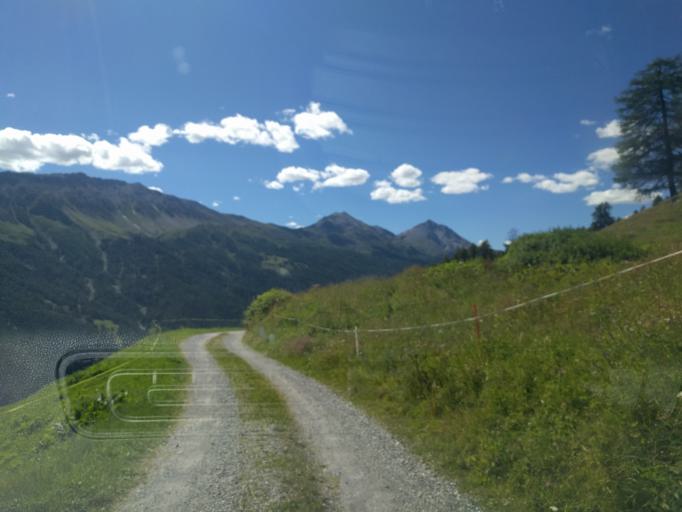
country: IT
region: Trentino-Alto Adige
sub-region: Bolzano
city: Tubre
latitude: 46.6103
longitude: 10.4090
